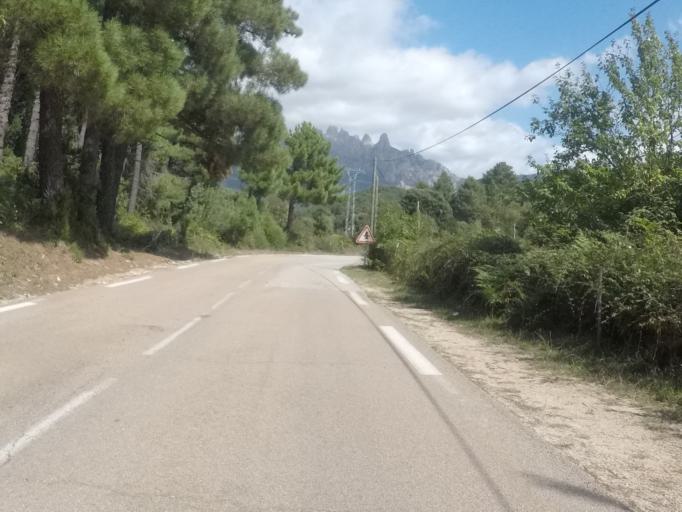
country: FR
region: Corsica
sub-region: Departement de la Corse-du-Sud
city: Zonza
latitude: 41.7589
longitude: 9.1833
